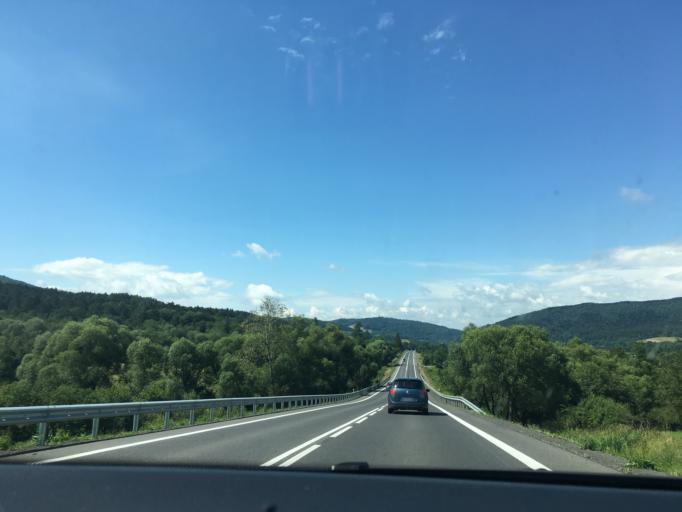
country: PL
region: Subcarpathian Voivodeship
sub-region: Powiat krosnienski
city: Dukla
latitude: 49.4926
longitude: 21.7032
